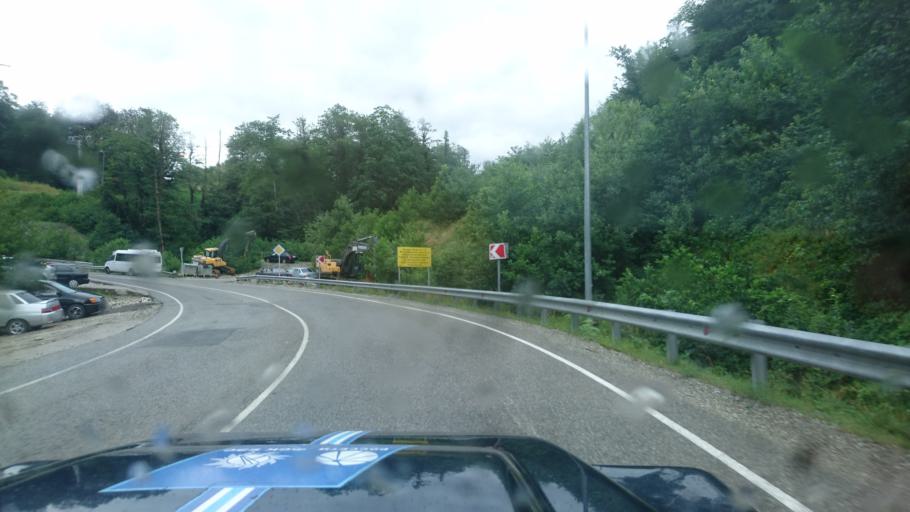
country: RU
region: Krasnodarskiy
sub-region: Sochi City
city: Krasnaya Polyana
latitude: 43.6739
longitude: 40.2840
